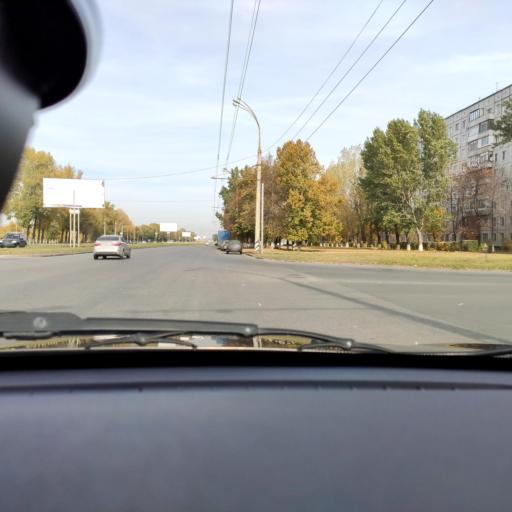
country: RU
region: Samara
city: Tol'yatti
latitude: 53.5167
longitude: 49.2584
